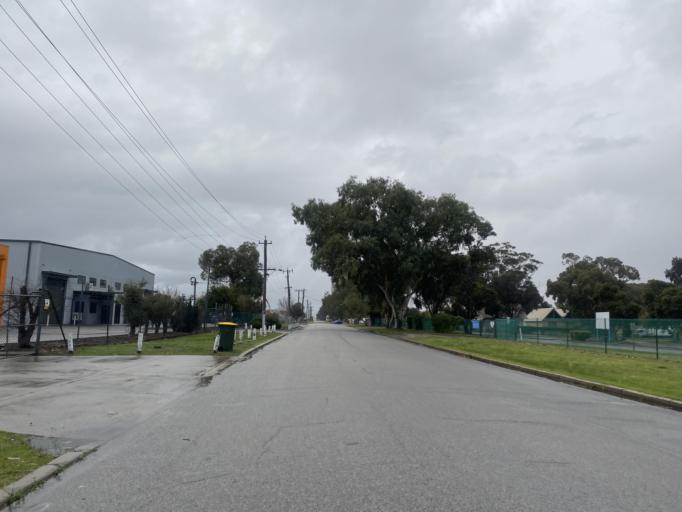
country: AU
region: Western Australia
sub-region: Canning
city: Queens Park
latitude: -31.9974
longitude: 115.9566
